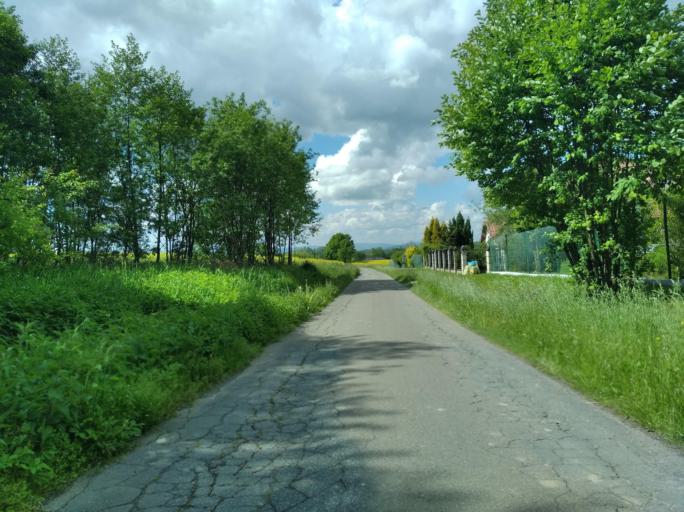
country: PL
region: Subcarpathian Voivodeship
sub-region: Powiat krosnienski
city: Korczyna
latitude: 49.7196
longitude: 21.8320
